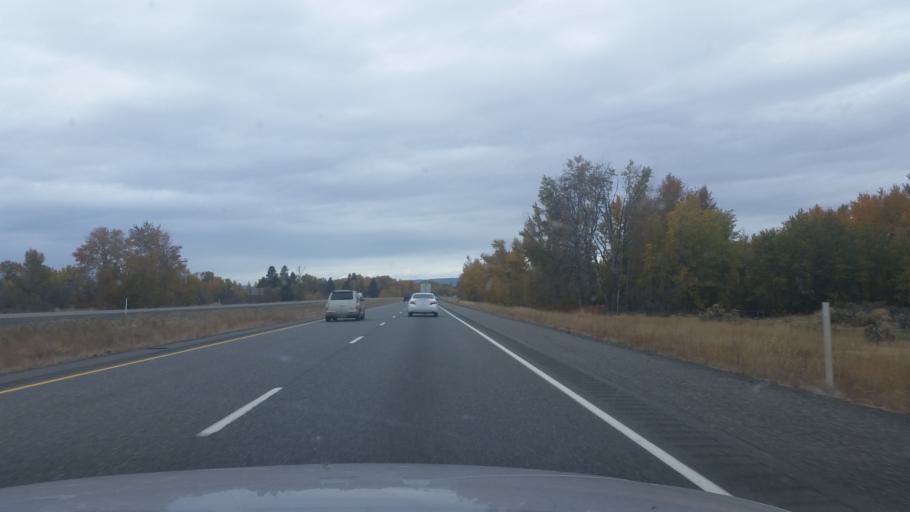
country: US
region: Washington
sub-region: Kittitas County
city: Ellensburg
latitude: 47.0286
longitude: -120.6190
